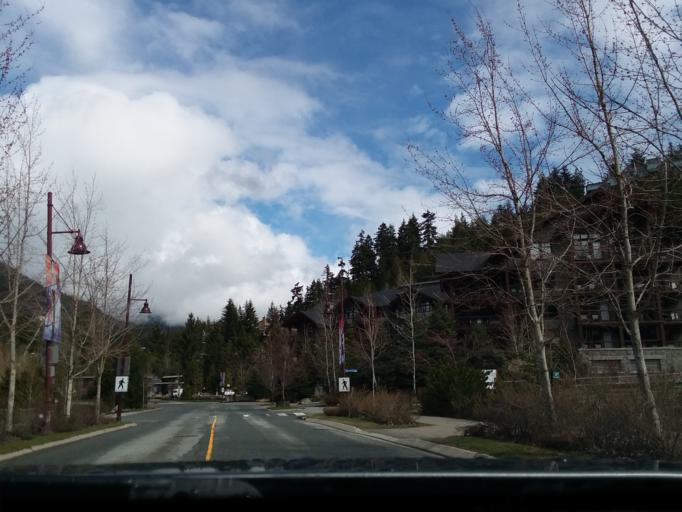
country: CA
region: British Columbia
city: Whistler
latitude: 50.0951
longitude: -122.9895
